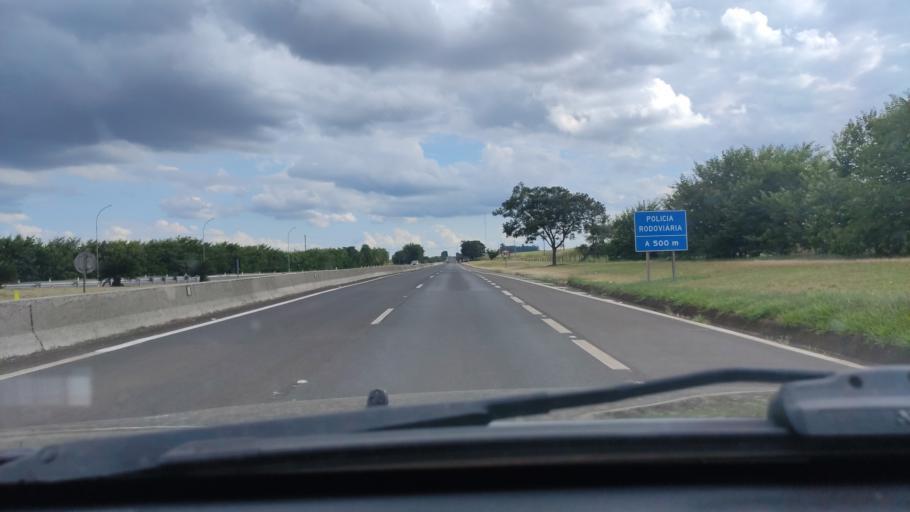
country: BR
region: Sao Paulo
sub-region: Santa Cruz Do Rio Pardo
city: Santa Cruz do Rio Pardo
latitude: -22.8066
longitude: -49.5336
